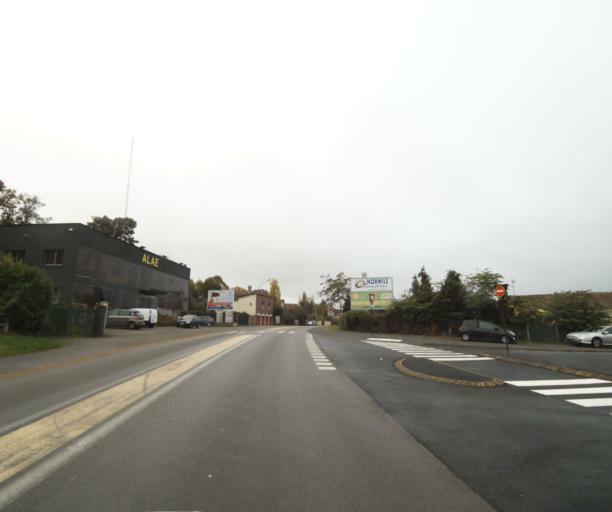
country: FR
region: Centre
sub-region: Departement d'Eure-et-Loir
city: Dreux
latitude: 48.7398
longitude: 1.3863
